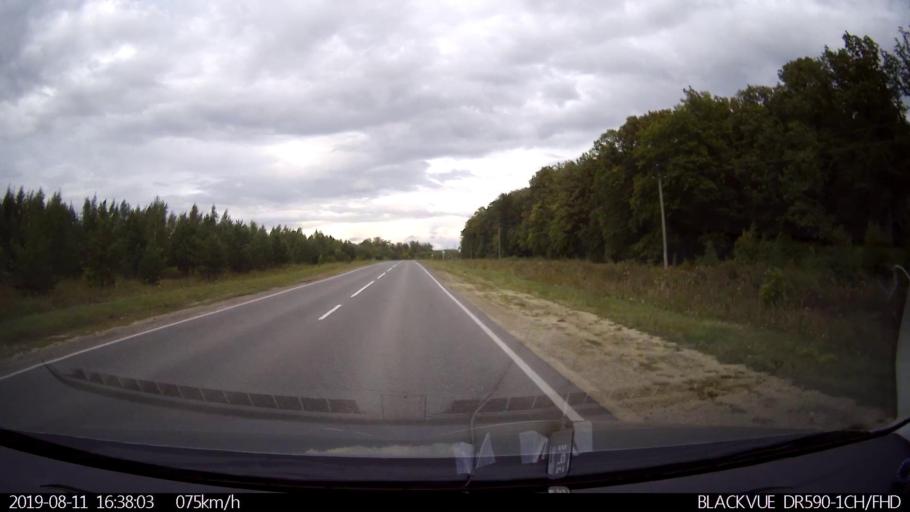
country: RU
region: Ulyanovsk
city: Mayna
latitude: 54.1317
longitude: 47.6194
